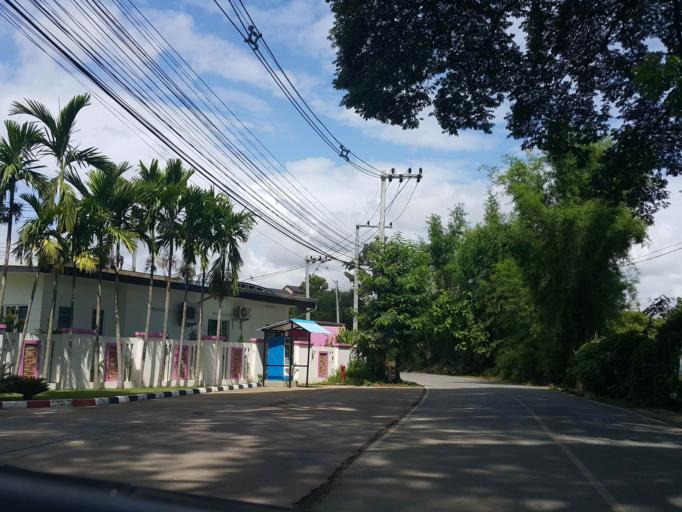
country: TH
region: Chiang Mai
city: Saraphi
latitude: 18.7433
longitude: 99.0619
